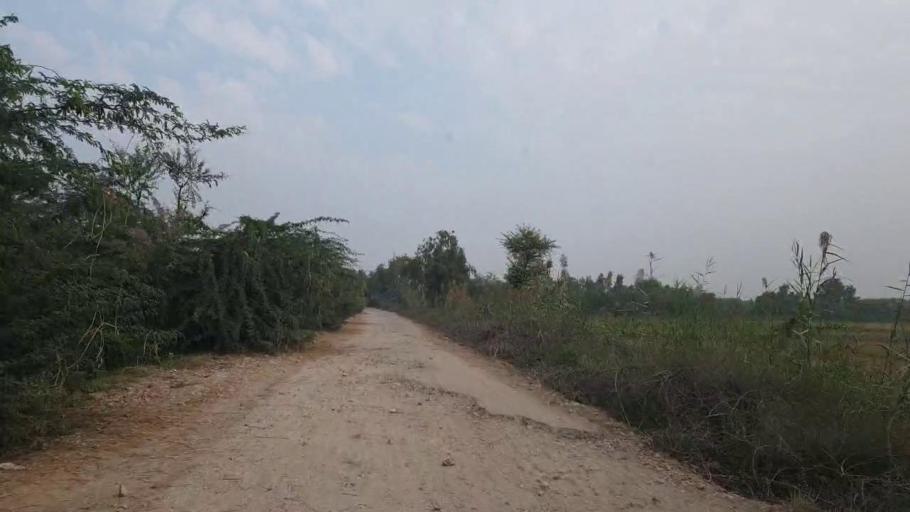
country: PK
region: Sindh
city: Talhar
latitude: 24.8322
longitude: 68.8805
